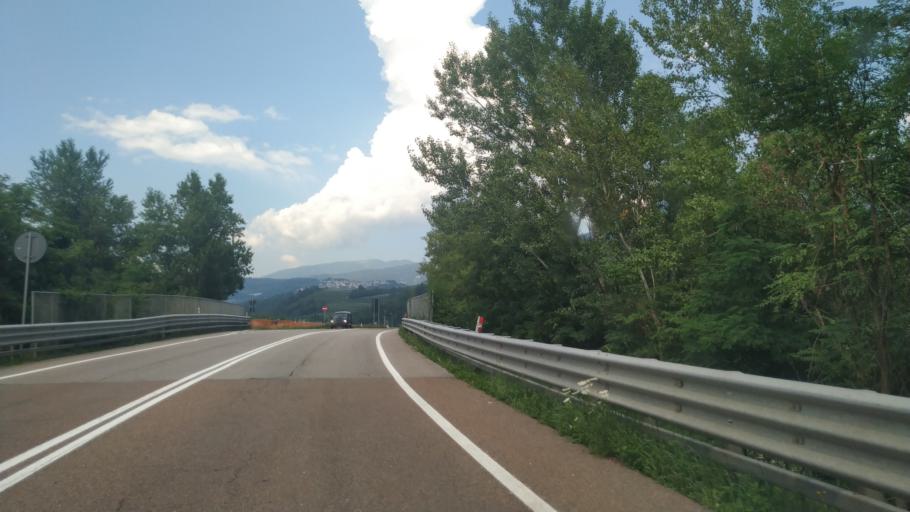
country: IT
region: Trentino-Alto Adige
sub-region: Provincia di Trento
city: Denno
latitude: 46.2631
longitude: 11.0581
